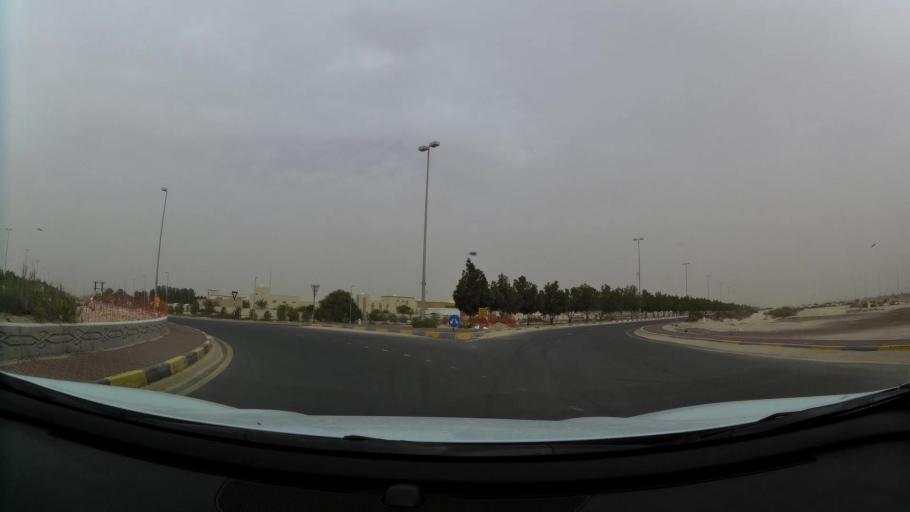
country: AE
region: Abu Dhabi
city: Abu Dhabi
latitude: 24.3610
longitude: 54.7172
